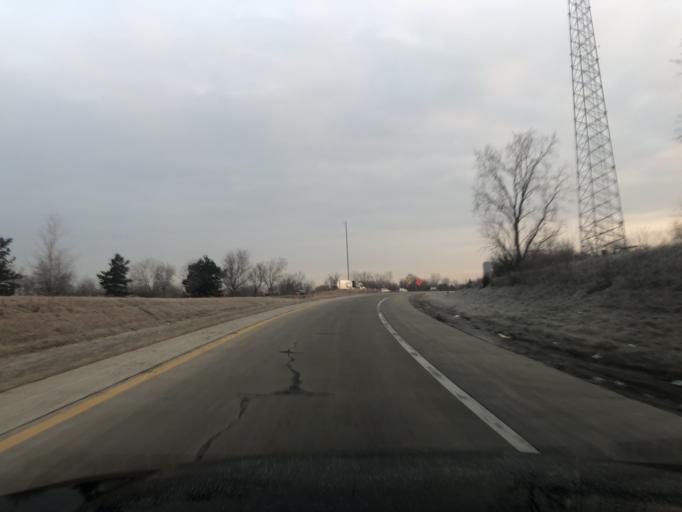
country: US
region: Michigan
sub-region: Wayne County
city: Romulus
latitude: 42.2271
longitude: -83.3852
